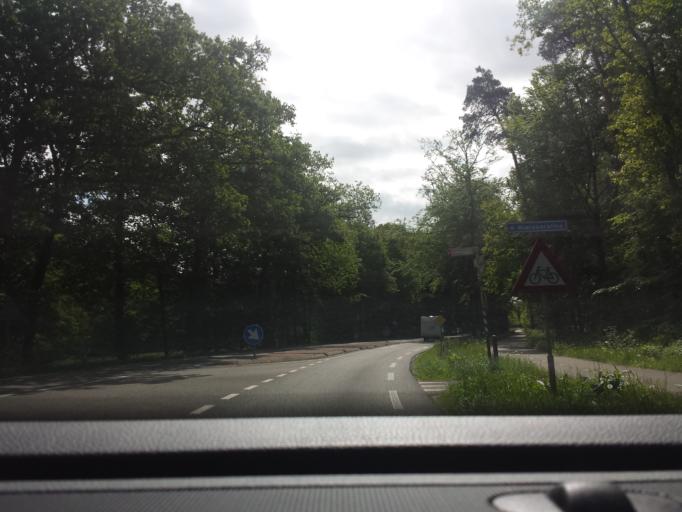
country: NL
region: Gelderland
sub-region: Gemeente Lochem
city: Barchem
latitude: 52.0967
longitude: 6.3924
